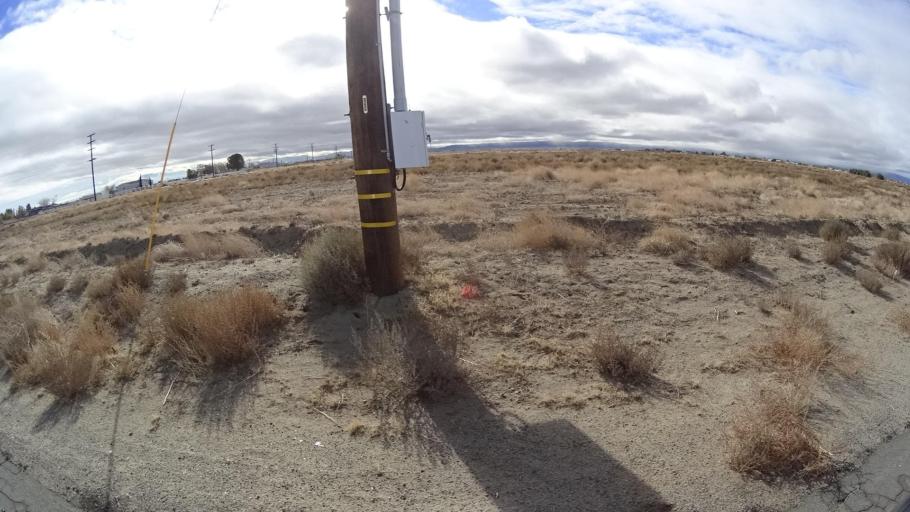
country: US
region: California
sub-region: Kern County
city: Rosamond
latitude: 34.8347
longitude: -118.2386
